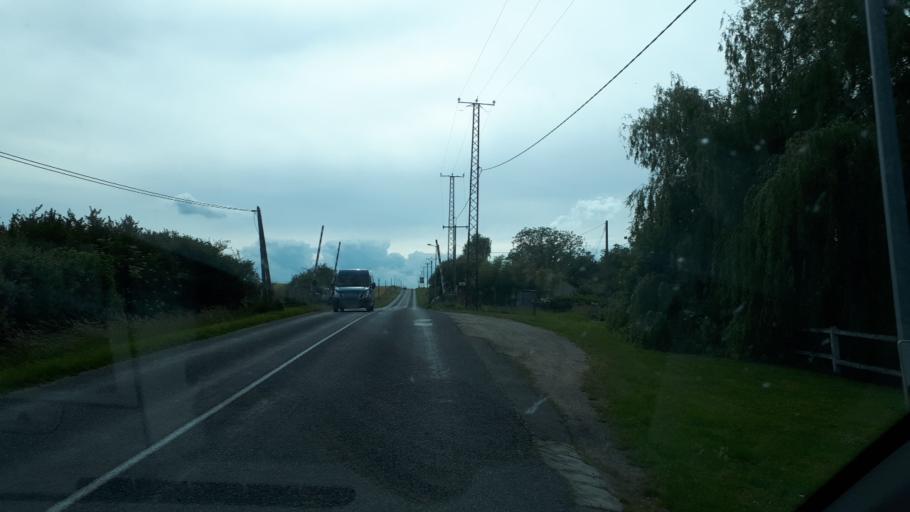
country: FR
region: Centre
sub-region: Departement du Cher
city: La Chapelle-Saint-Ursin
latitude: 47.0803
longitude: 2.3154
